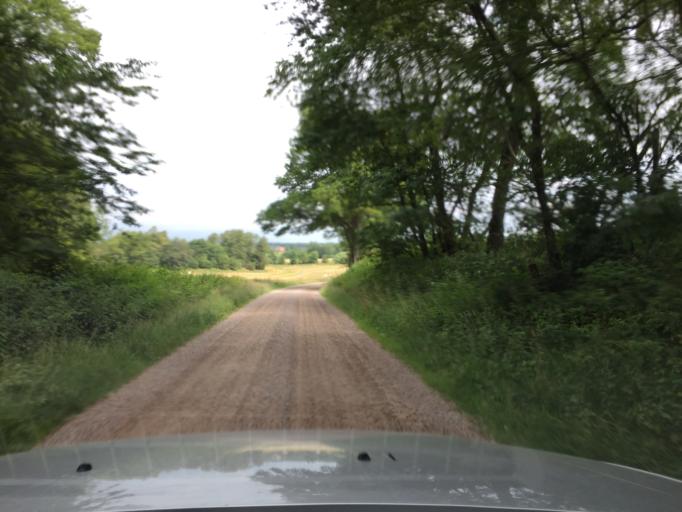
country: SE
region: Skane
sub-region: Hassleholms Kommun
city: Sosdala
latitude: 56.0218
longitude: 13.6805
